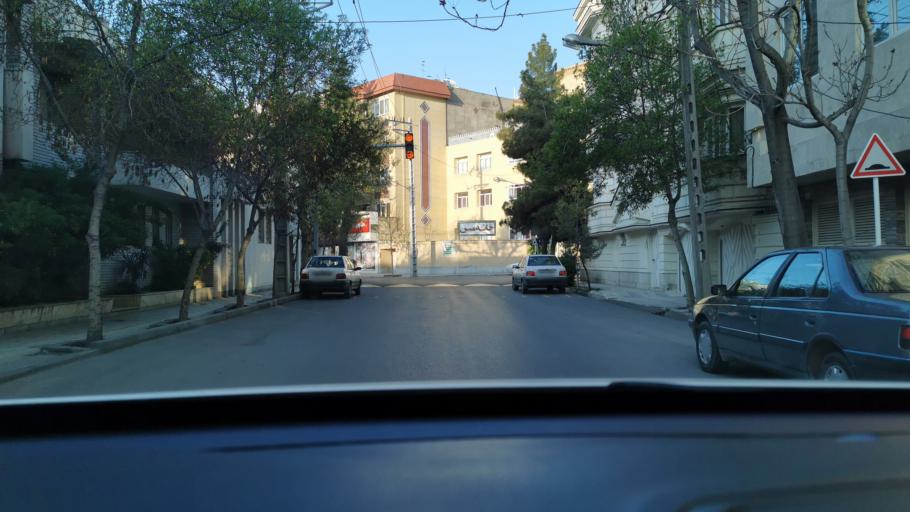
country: IR
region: Razavi Khorasan
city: Mashhad
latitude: 36.2997
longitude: 59.5811
